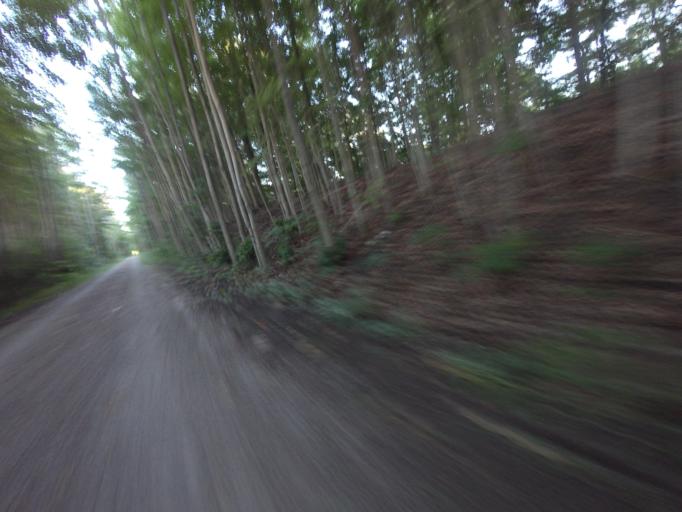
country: CA
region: Ontario
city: Goderich
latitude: 43.7599
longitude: -81.6922
